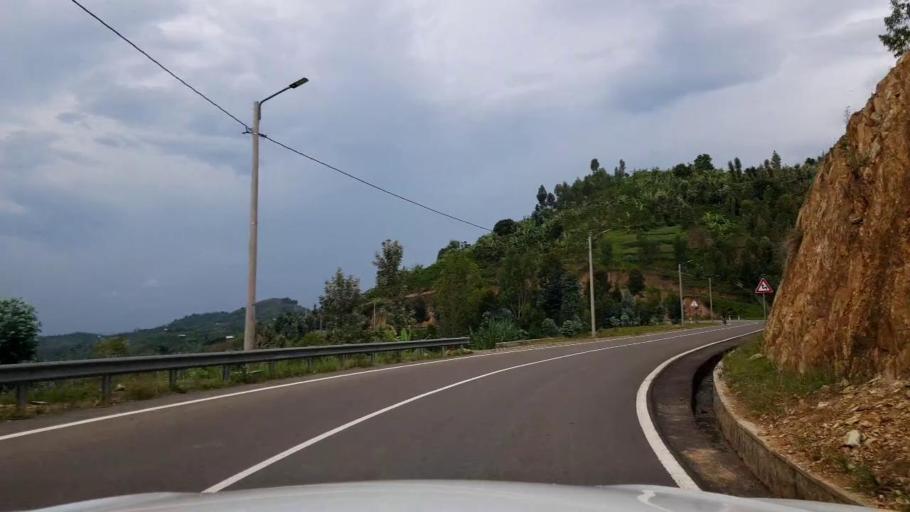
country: RW
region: Western Province
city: Kibuye
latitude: -2.0260
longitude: 29.3905
